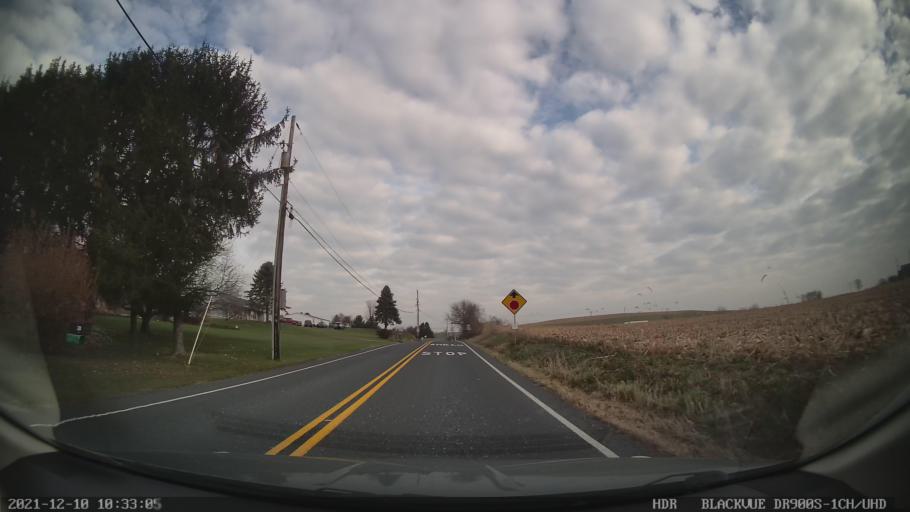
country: US
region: Pennsylvania
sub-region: Berks County
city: Topton
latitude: 40.5380
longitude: -75.7173
